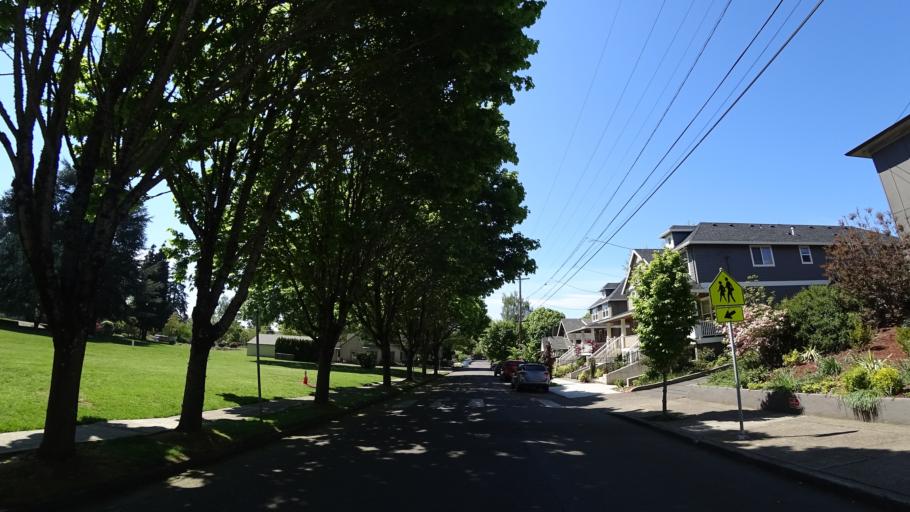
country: US
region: Oregon
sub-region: Clackamas County
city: Milwaukie
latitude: 45.4691
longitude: -122.6232
